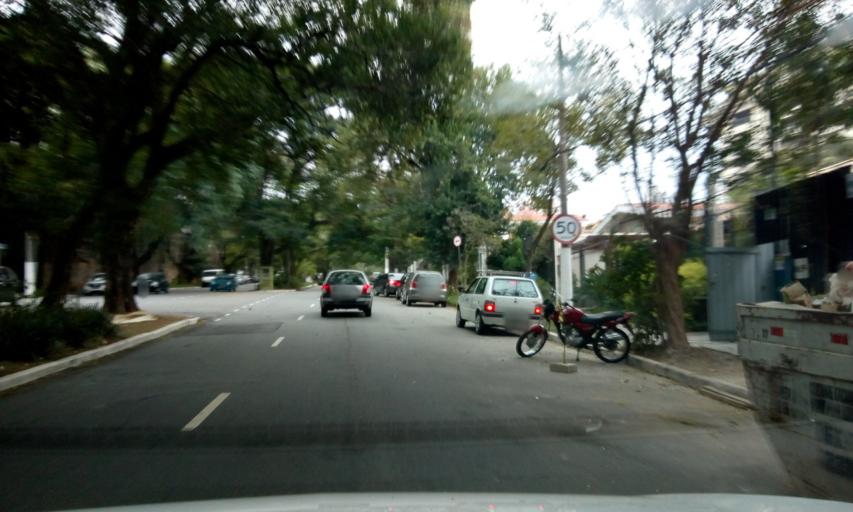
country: BR
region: Sao Paulo
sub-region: Osasco
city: Osasco
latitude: -23.5407
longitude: -46.7194
